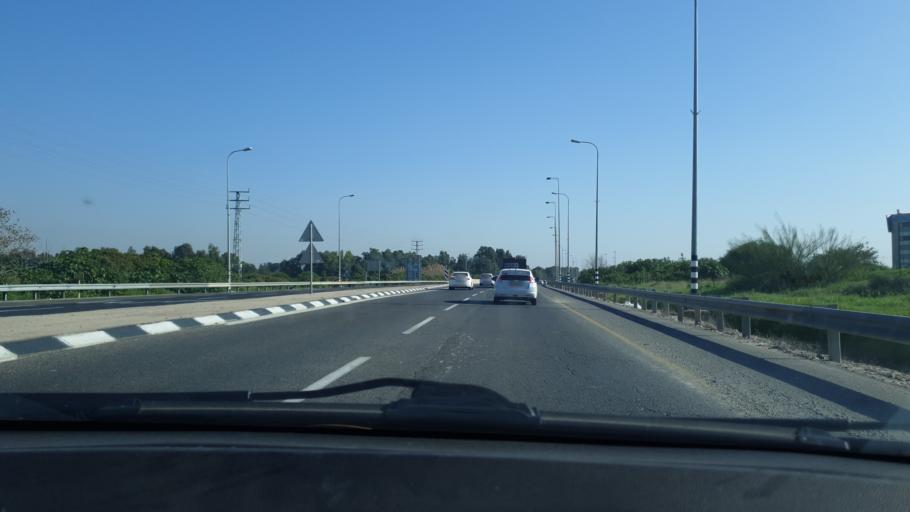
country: IL
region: Central District
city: Kefar Habad
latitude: 31.9589
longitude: 34.8522
